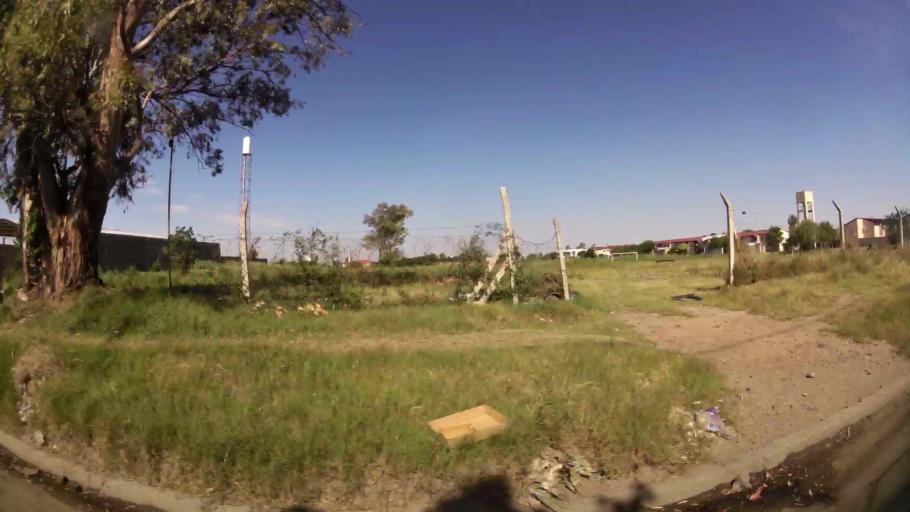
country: AR
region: Cordoba
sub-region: Departamento de Capital
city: Cordoba
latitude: -31.3628
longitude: -64.1838
